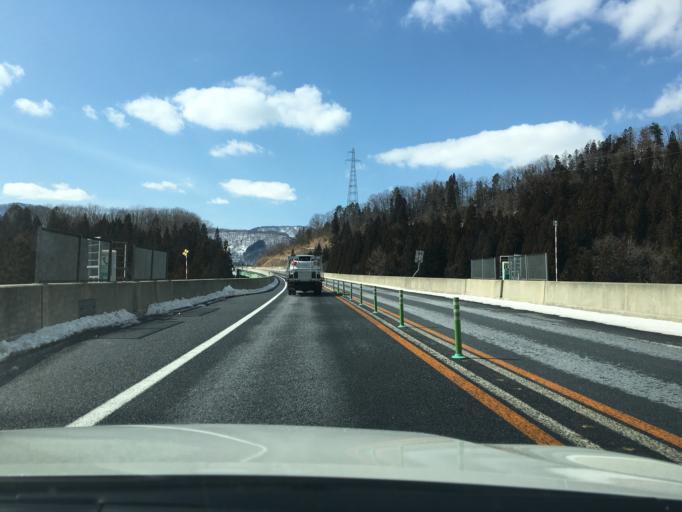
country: JP
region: Yamagata
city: Sagae
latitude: 38.4371
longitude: 140.0927
